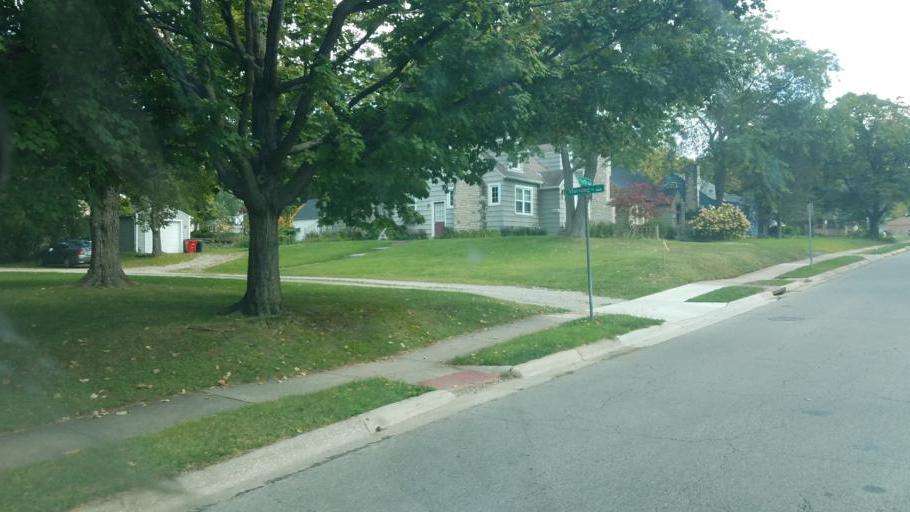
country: US
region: Ohio
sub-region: Franklin County
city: Worthington
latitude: 40.0928
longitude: -83.0140
